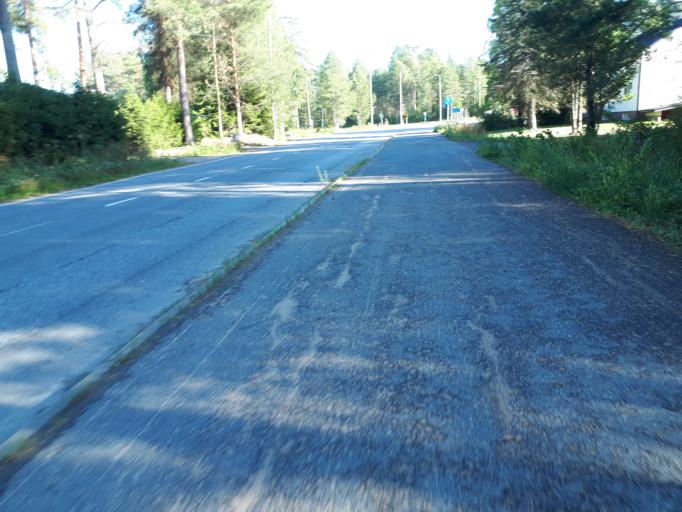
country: FI
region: Northern Ostrobothnia
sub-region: Oulunkaari
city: Ii
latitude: 65.3172
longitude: 25.3863
